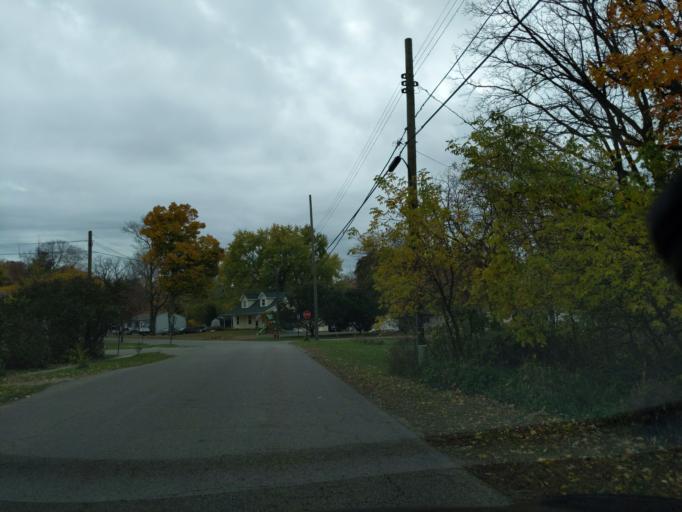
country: US
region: Michigan
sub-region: Eaton County
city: Eaton Rapids
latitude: 42.5159
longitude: -84.6501
